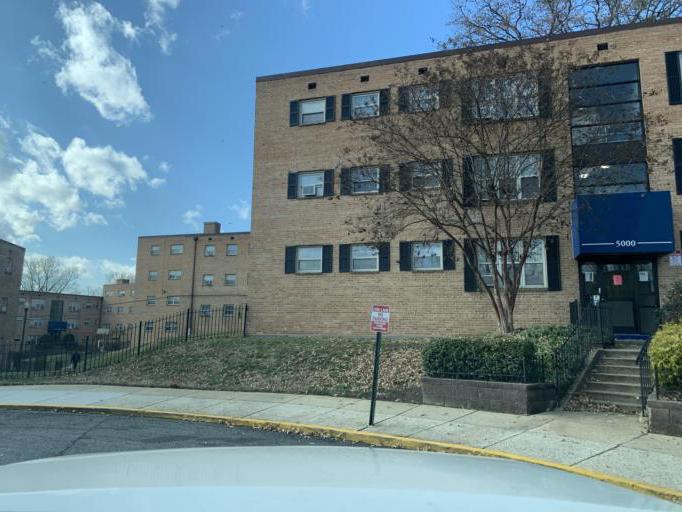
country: US
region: Maryland
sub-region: Prince George's County
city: Fairmount Heights
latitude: 38.9014
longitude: -76.9295
